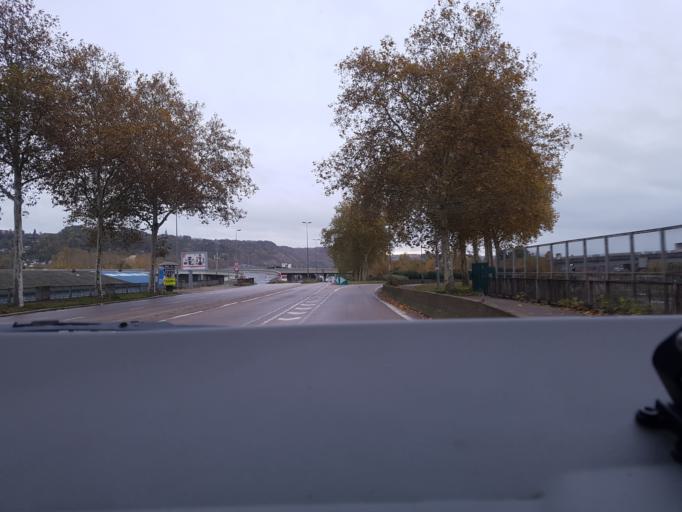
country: FR
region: Haute-Normandie
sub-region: Departement de la Seine-Maritime
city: Rouen
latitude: 49.4314
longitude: 1.0981
